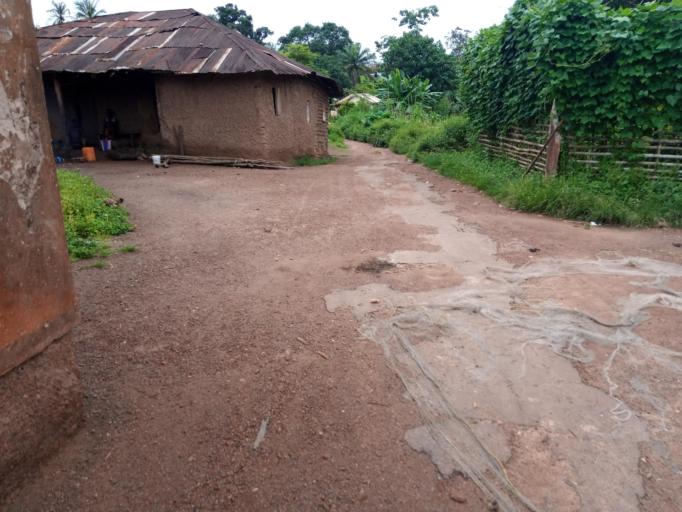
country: SL
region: Southern Province
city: Largo
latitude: 8.2046
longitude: -12.0624
